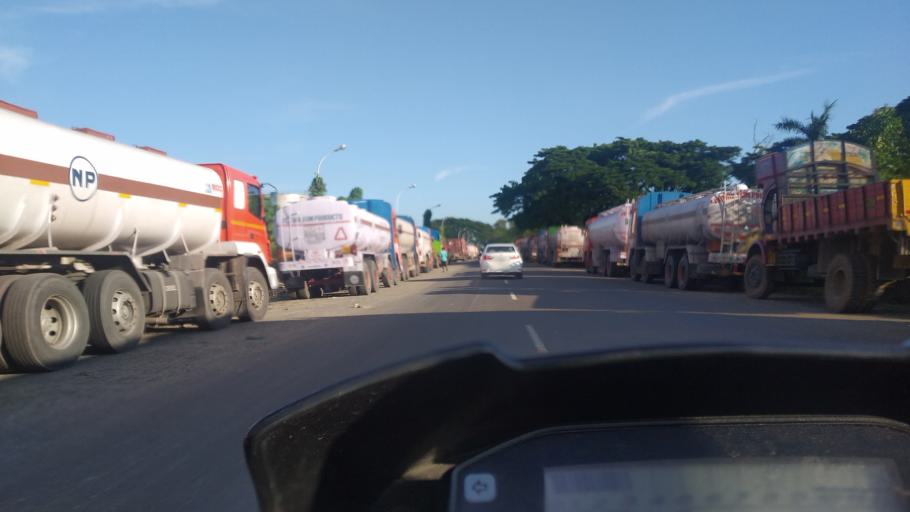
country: IN
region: Kerala
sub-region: Ernakulam
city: Cochin
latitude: 9.9382
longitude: 76.2697
